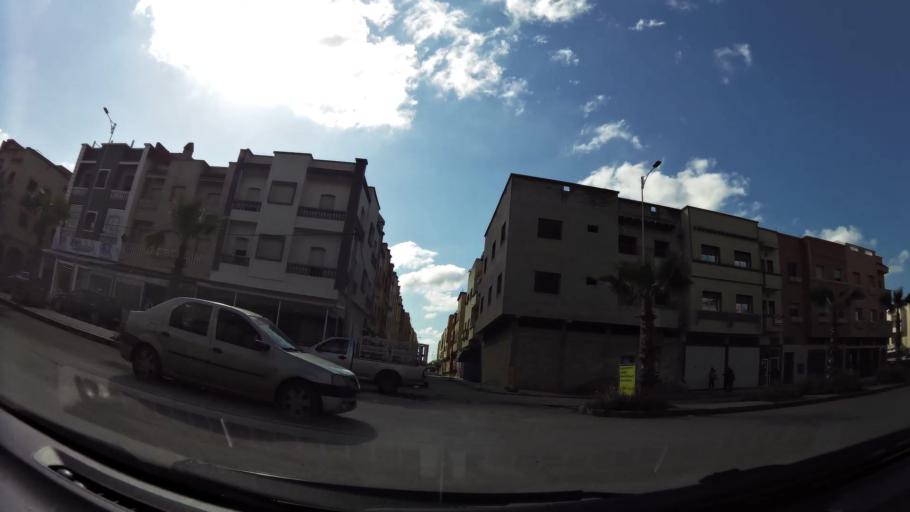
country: MA
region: Grand Casablanca
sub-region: Mediouna
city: Mediouna
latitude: 33.3839
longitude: -7.5335
